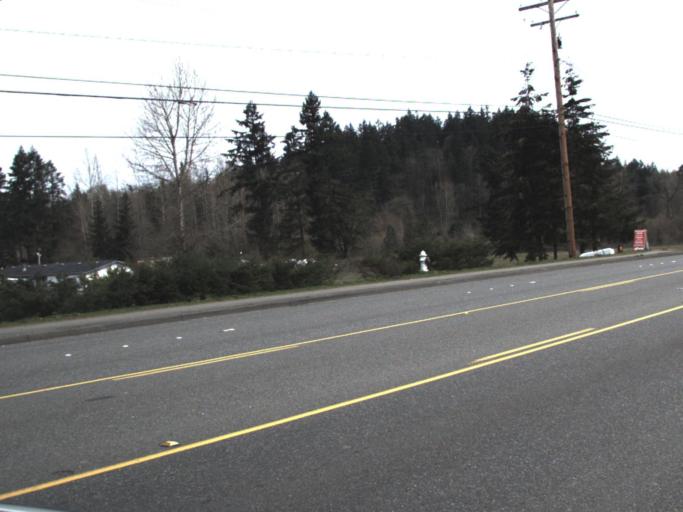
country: US
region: Washington
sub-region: King County
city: Covington
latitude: 47.3580
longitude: -122.1348
